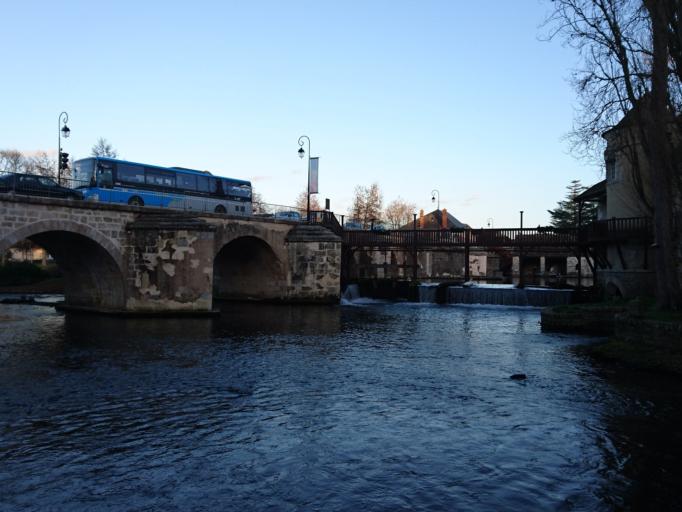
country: FR
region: Ile-de-France
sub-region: Departement de Seine-et-Marne
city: Moret-sur-Loing
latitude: 48.3724
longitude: 2.8190
